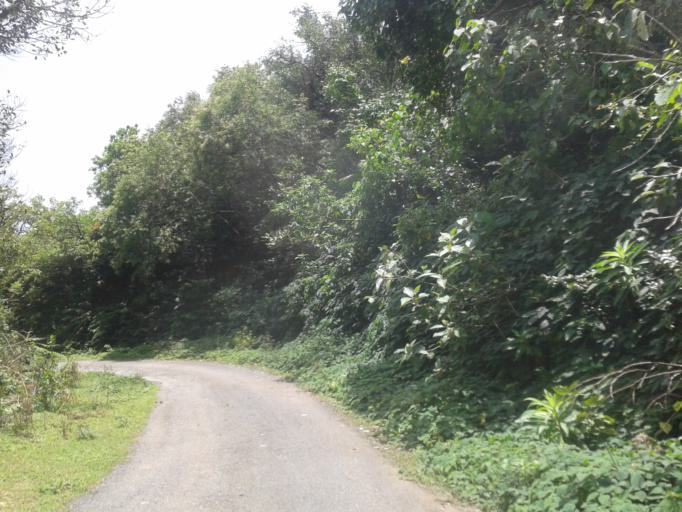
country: IN
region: Karnataka
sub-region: Chikmagalur
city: Mudigere
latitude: 12.9864
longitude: 75.6046
